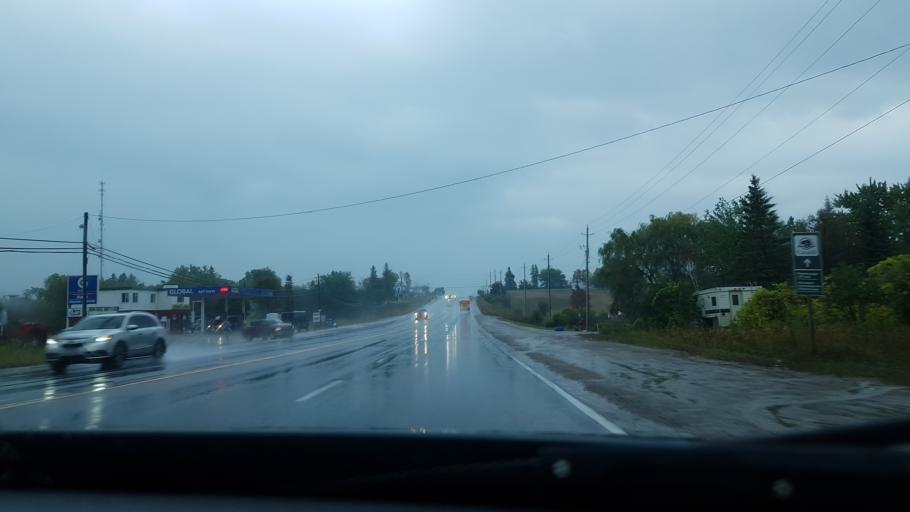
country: CA
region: Ontario
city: Peterborough
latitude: 44.3474
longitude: -78.3601
